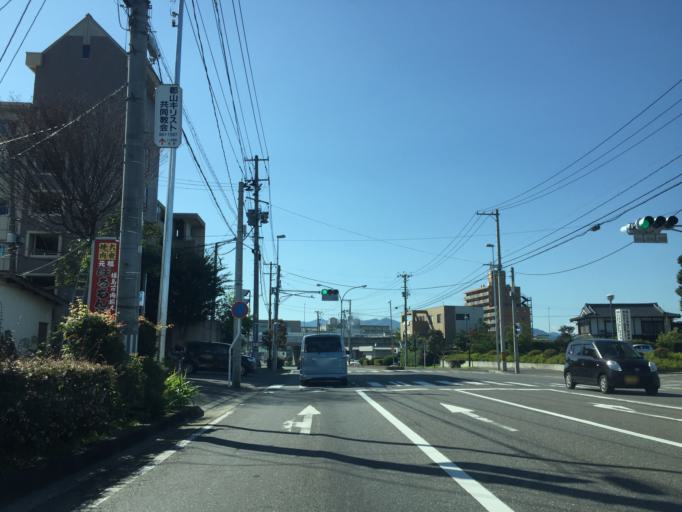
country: JP
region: Fukushima
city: Koriyama
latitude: 37.4077
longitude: 140.3455
